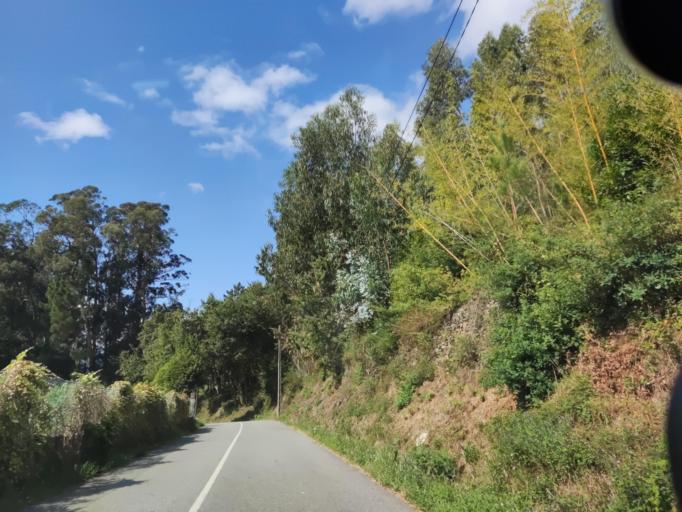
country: ES
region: Galicia
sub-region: Provincia da Coruna
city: Boiro
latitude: 42.6224
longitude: -8.8724
